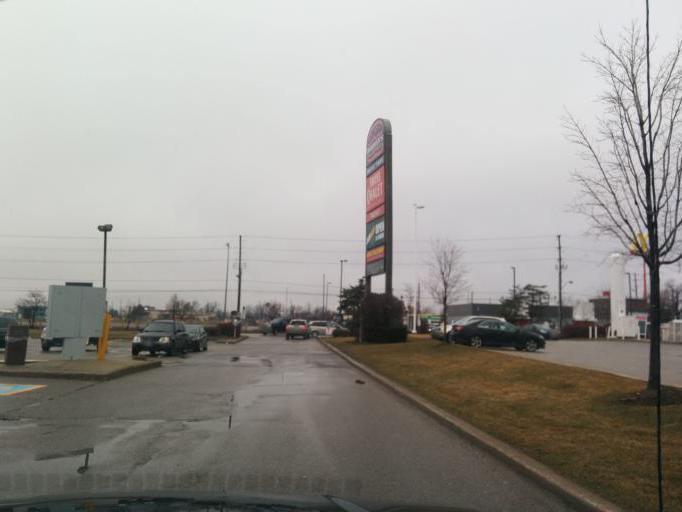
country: CA
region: Ontario
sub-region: Halton
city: Milton
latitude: 43.5229
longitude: -79.9000
